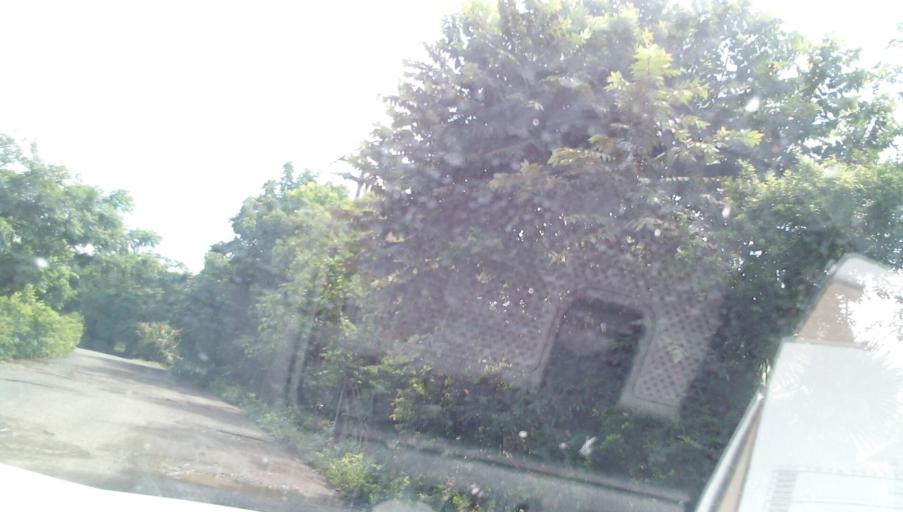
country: MX
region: Veracruz
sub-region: Alamo Temapache
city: Vegas de la Soledad y Soledad Dos
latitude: 20.9052
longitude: -97.9317
